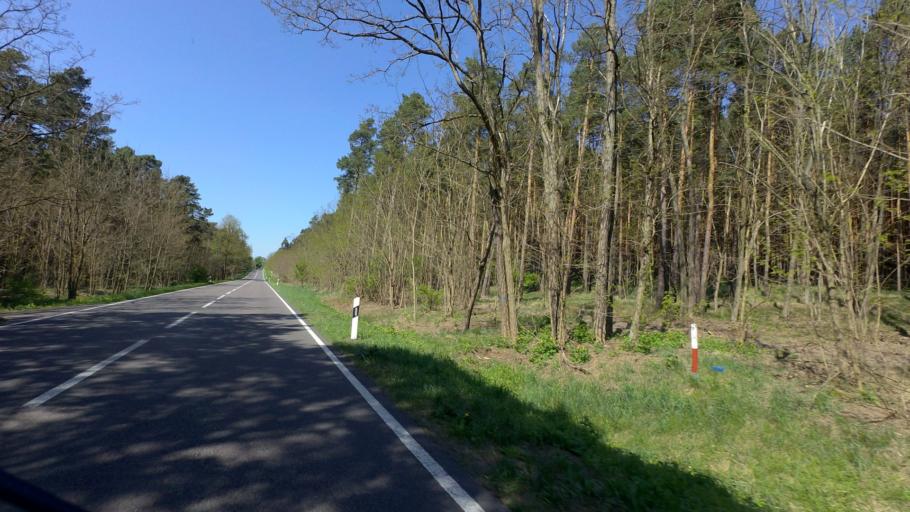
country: DE
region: Brandenburg
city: Lieberose
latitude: 52.0324
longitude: 14.2992
